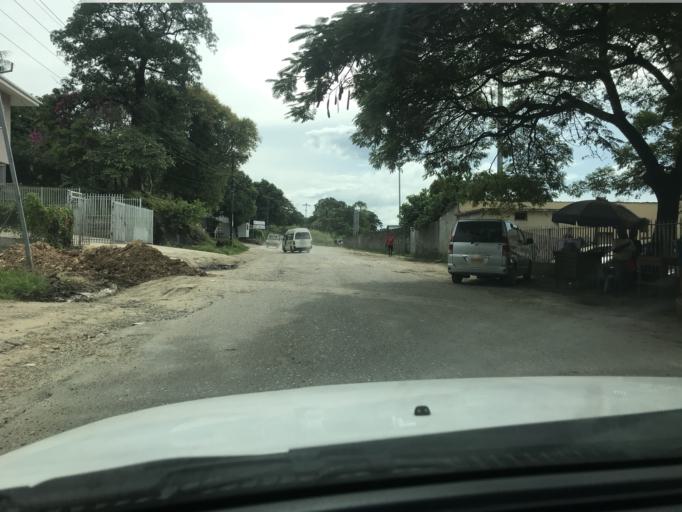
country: SB
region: Guadalcanal
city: Honiara
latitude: -9.4316
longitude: 159.9495
